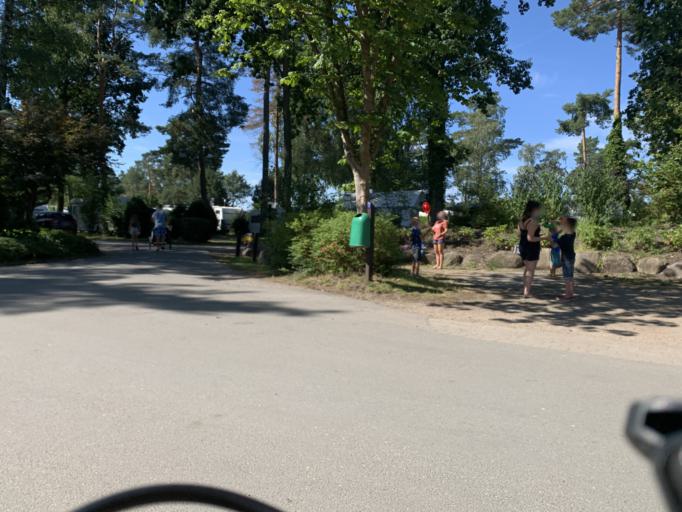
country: DE
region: Lower Saxony
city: Wietzendorf
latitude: 52.9351
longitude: 9.9662
